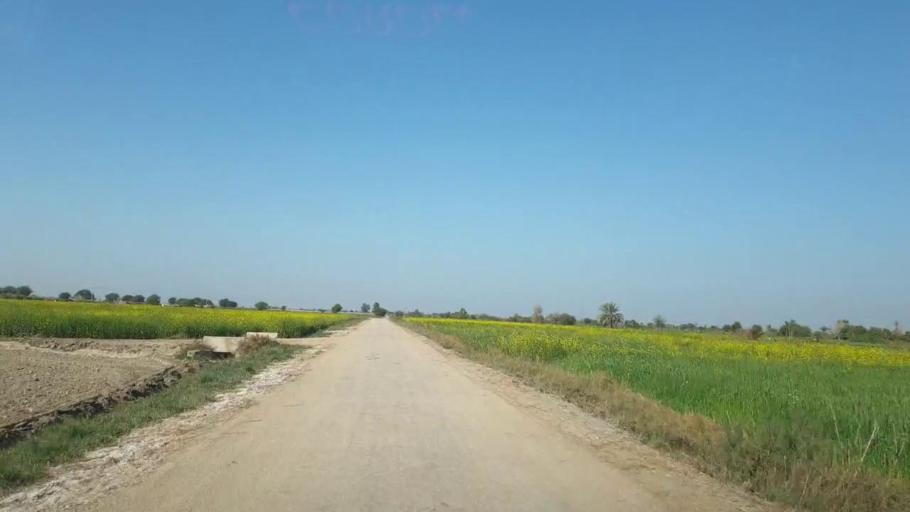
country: PK
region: Sindh
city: Mirpur Khas
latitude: 25.6368
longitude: 69.0434
